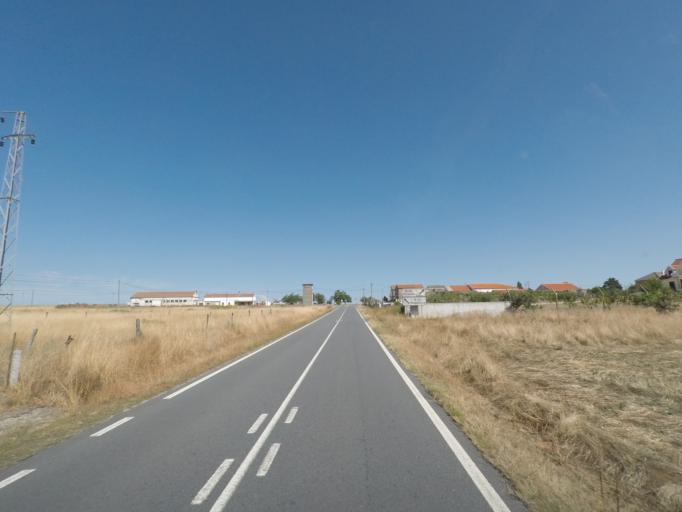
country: ES
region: Castille and Leon
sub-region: Provincia de Salamanca
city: Villarino de los Aires
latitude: 41.3655
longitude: -6.4963
